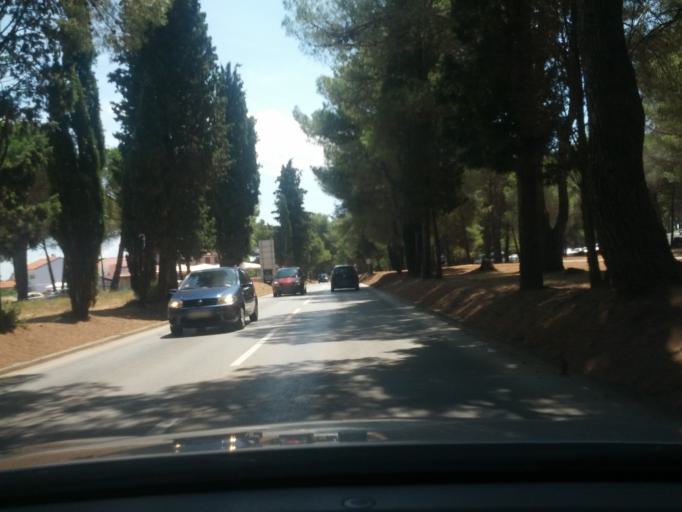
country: HR
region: Istarska
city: Fazana
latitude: 44.9179
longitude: 13.8117
